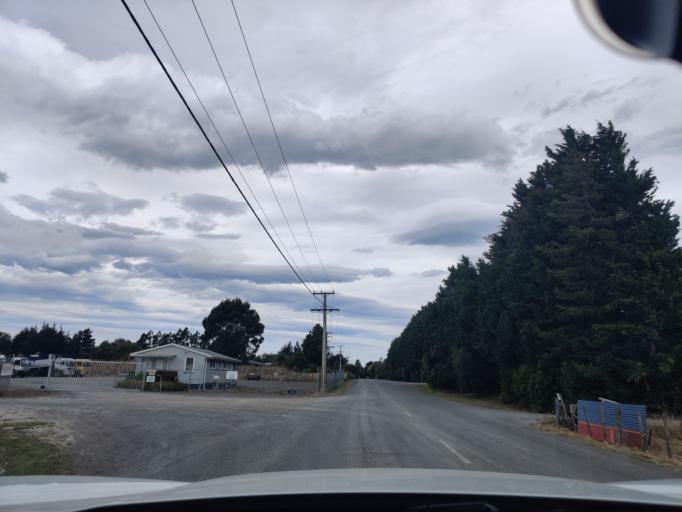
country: NZ
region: Wellington
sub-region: Masterton District
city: Masterton
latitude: -41.0407
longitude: 175.5025
